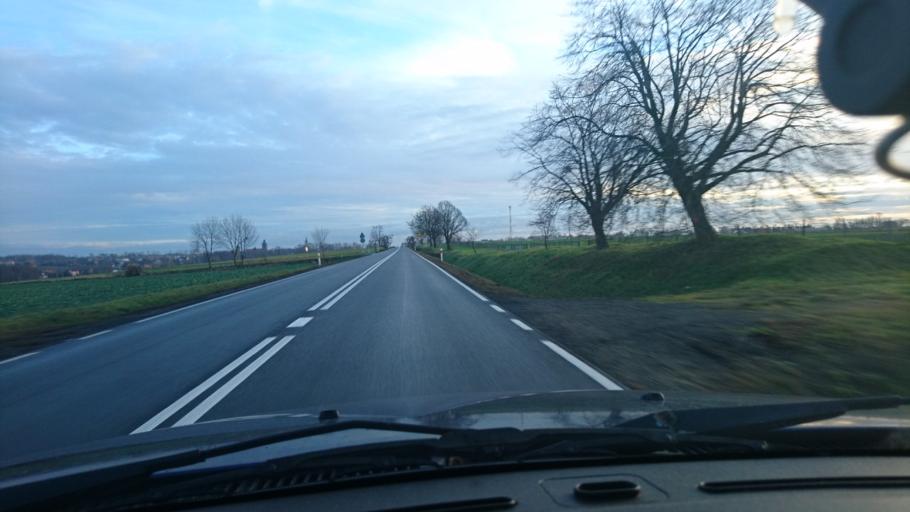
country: PL
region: Opole Voivodeship
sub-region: Powiat kluczborski
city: Byczyna
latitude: 51.1244
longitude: 18.2039
